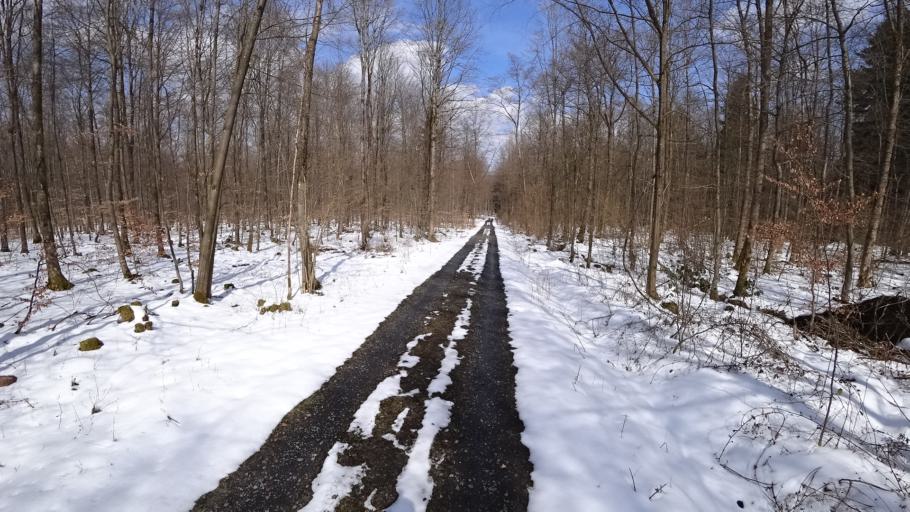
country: DE
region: Rheinland-Pfalz
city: Dickendorf
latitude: 50.7295
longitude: 7.8549
